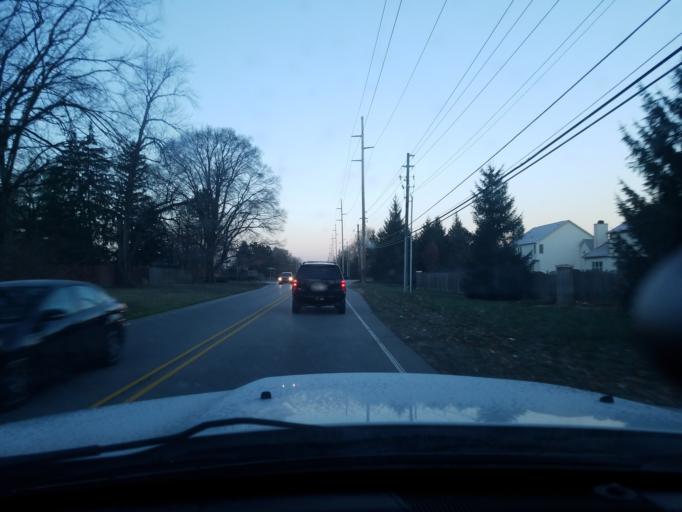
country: US
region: Indiana
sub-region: Marion County
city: Meridian Hills
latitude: 39.8971
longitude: -86.2229
